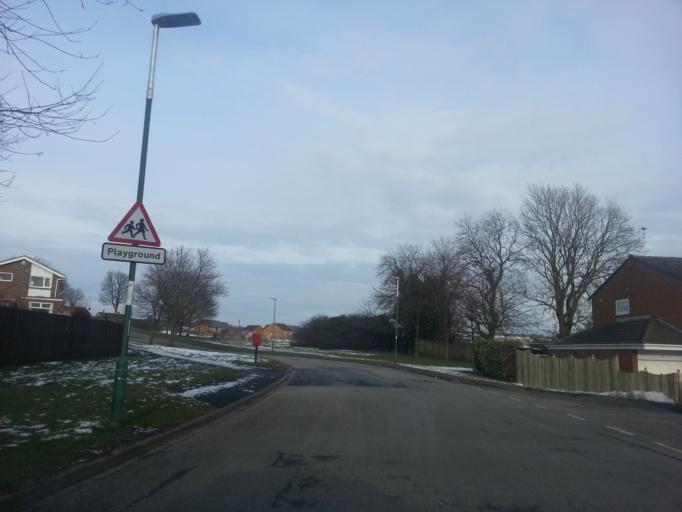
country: GB
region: England
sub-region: County Durham
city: Crook
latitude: 54.7101
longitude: -1.7574
